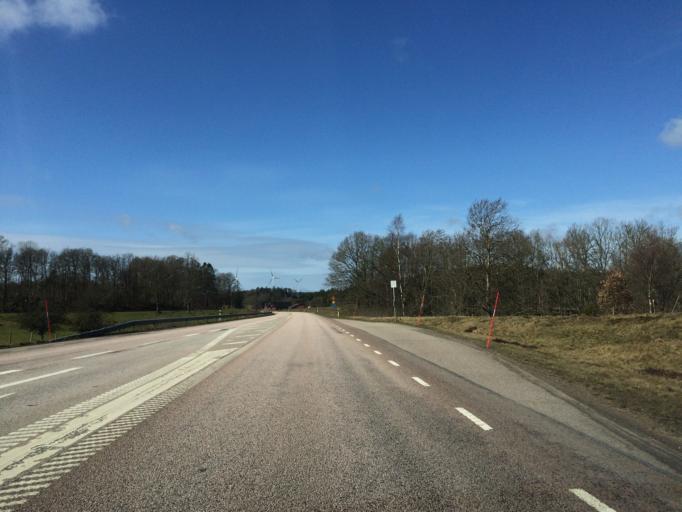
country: SE
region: Halland
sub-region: Laholms Kommun
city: Knared
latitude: 56.5254
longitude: 13.2469
